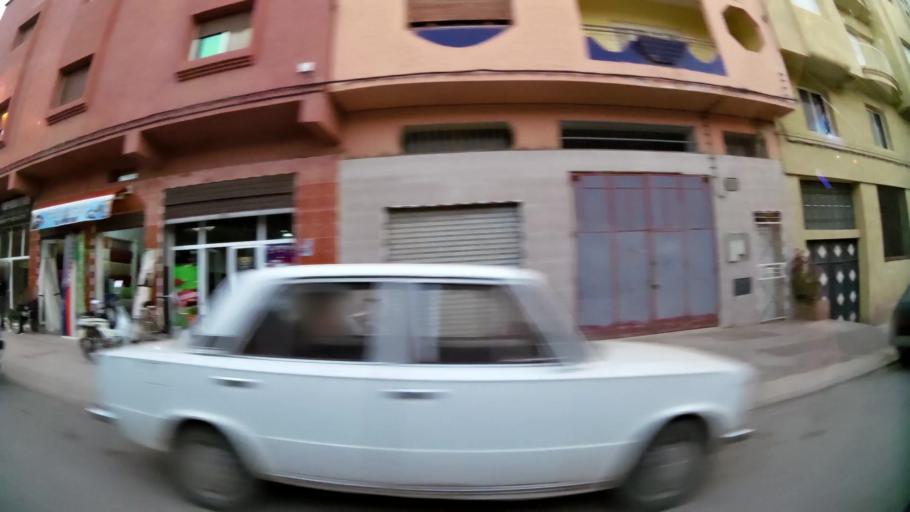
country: MA
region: Oriental
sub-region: Berkane-Taourirt
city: Berkane
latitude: 34.9242
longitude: -2.3315
